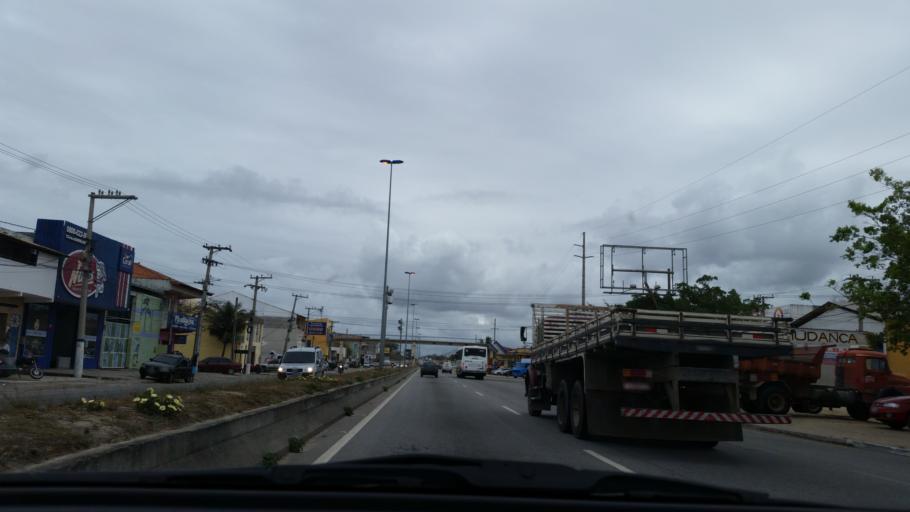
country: BR
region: Rio de Janeiro
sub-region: Sao Pedro Da Aldeia
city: Sao Pedro da Aldeia
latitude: -22.8416
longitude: -42.0717
